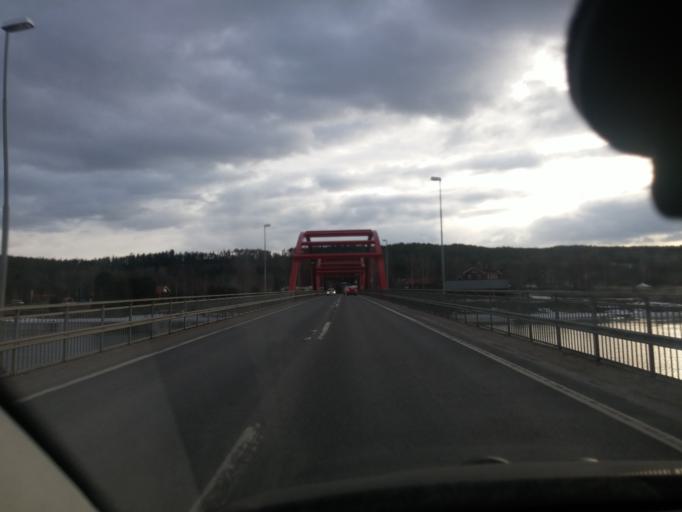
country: SE
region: Gaevleborg
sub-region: Ljusdals Kommun
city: Ljusdal
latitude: 61.8239
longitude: 16.0666
